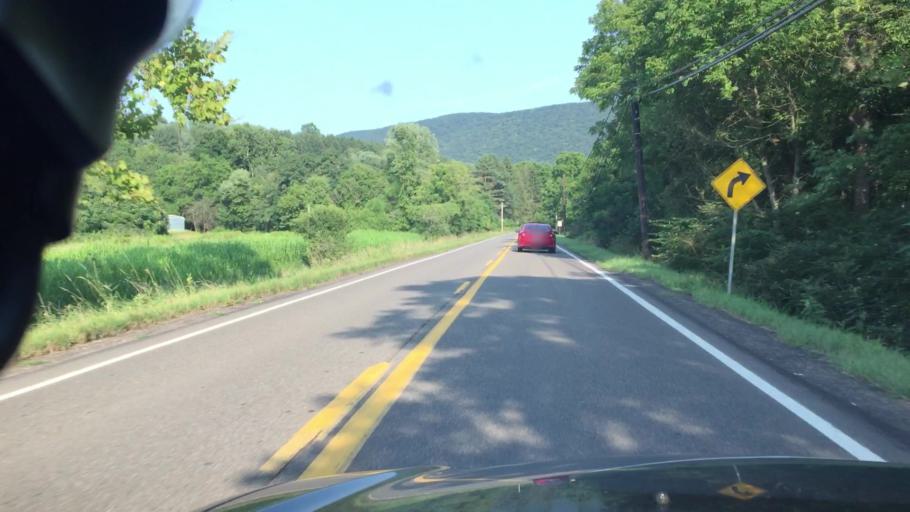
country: US
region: Pennsylvania
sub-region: Columbia County
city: Almedia
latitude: 40.9798
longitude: -76.3797
